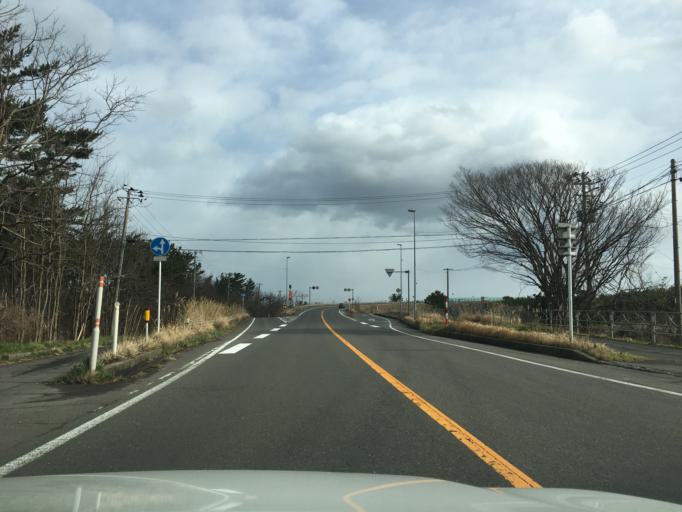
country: JP
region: Yamagata
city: Yuza
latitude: 39.2401
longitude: 139.9128
